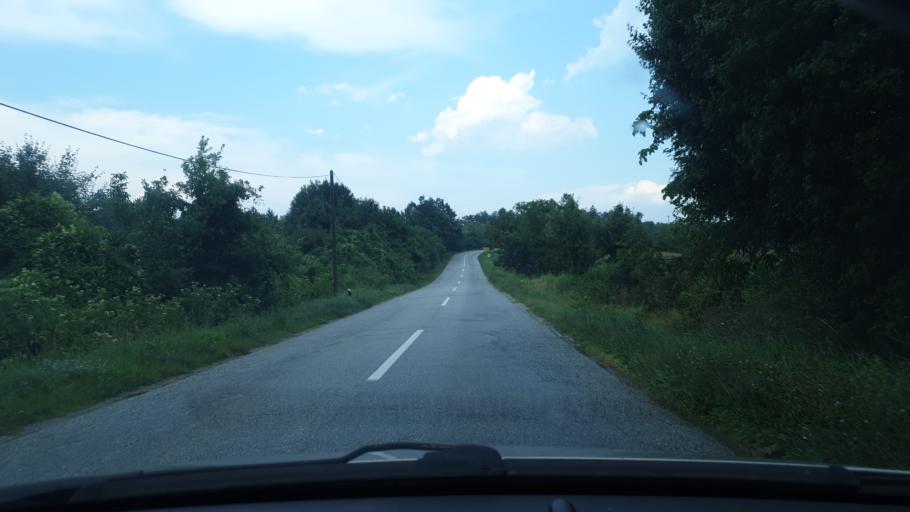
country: RS
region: Central Serbia
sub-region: Sumadijski Okrug
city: Kragujevac
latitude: 44.0450
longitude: 20.7904
